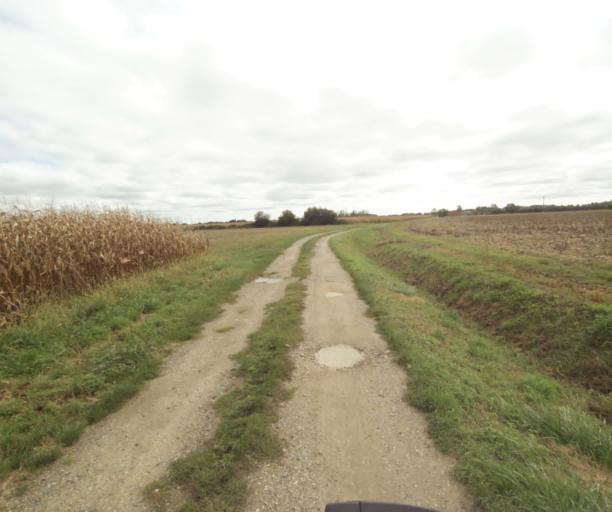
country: FR
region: Midi-Pyrenees
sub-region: Departement du Tarn-et-Garonne
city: Montech
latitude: 43.9711
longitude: 1.2009
